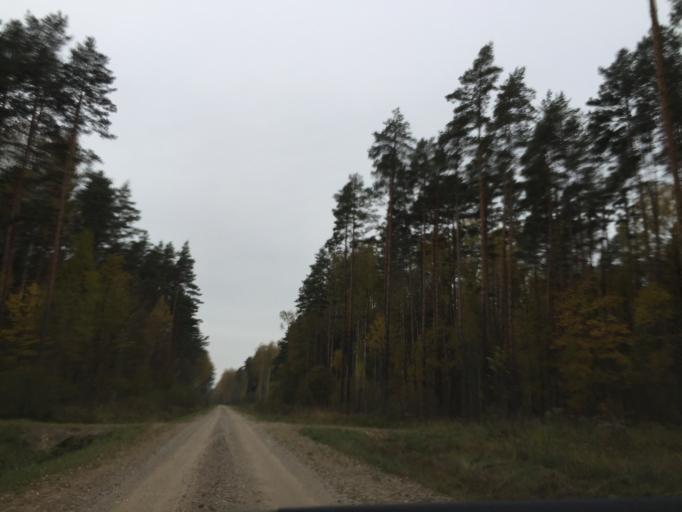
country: LV
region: Jelgava
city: Jelgava
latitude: 56.6371
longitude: 23.6341
